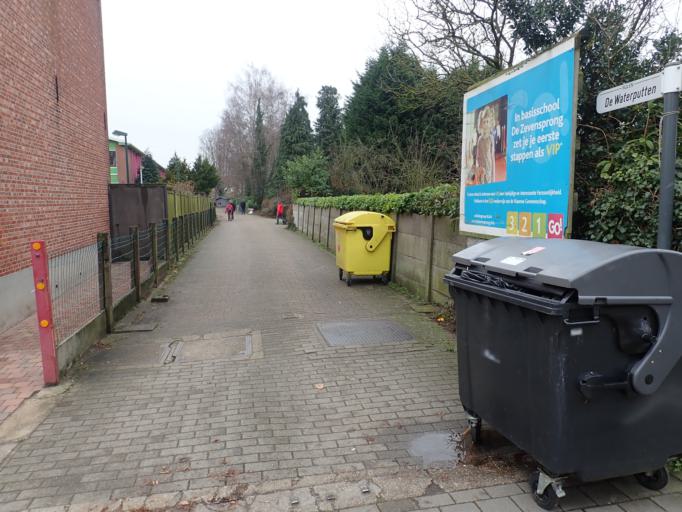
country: BE
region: Flanders
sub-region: Provincie Antwerpen
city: Nijlen
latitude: 51.1632
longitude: 4.6706
